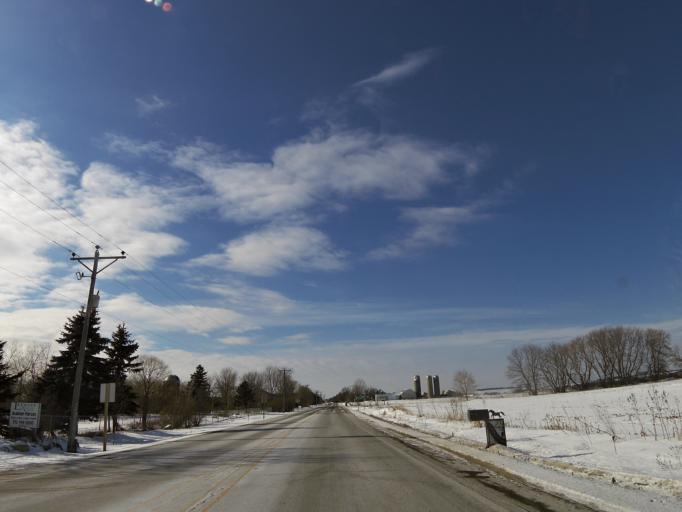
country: US
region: Wisconsin
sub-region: Saint Croix County
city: Roberts
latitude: 44.9926
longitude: -92.5616
